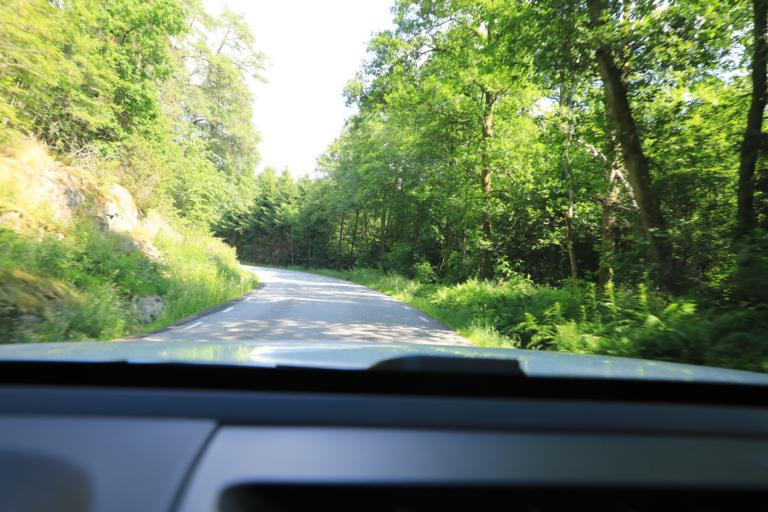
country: SE
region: Halland
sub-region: Varbergs Kommun
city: Veddige
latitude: 57.2050
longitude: 12.3411
